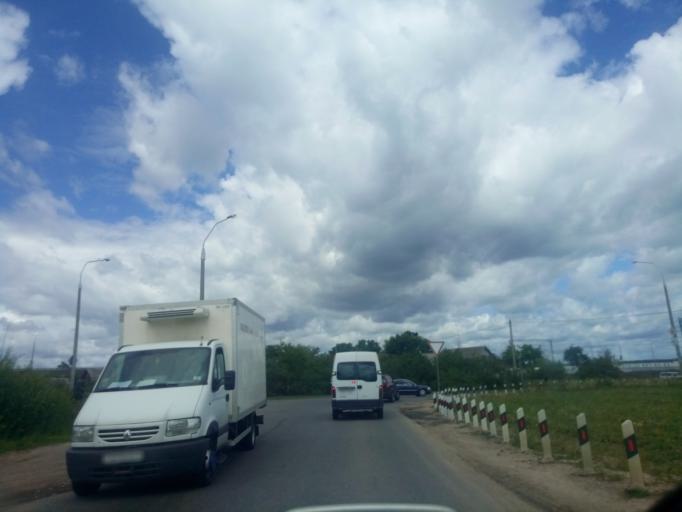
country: BY
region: Minsk
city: Zhdanovichy
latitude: 53.9403
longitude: 27.4360
